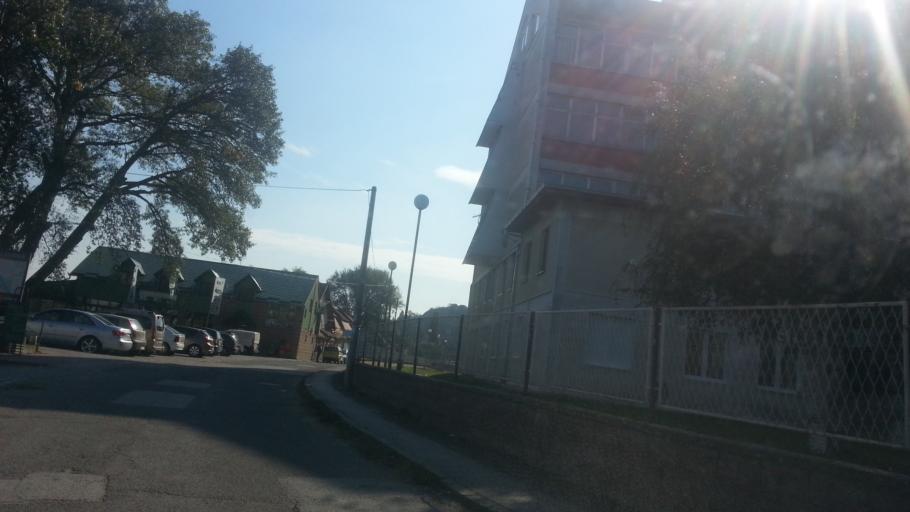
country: RS
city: Novi Slankamen
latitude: 45.1401
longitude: 20.2602
